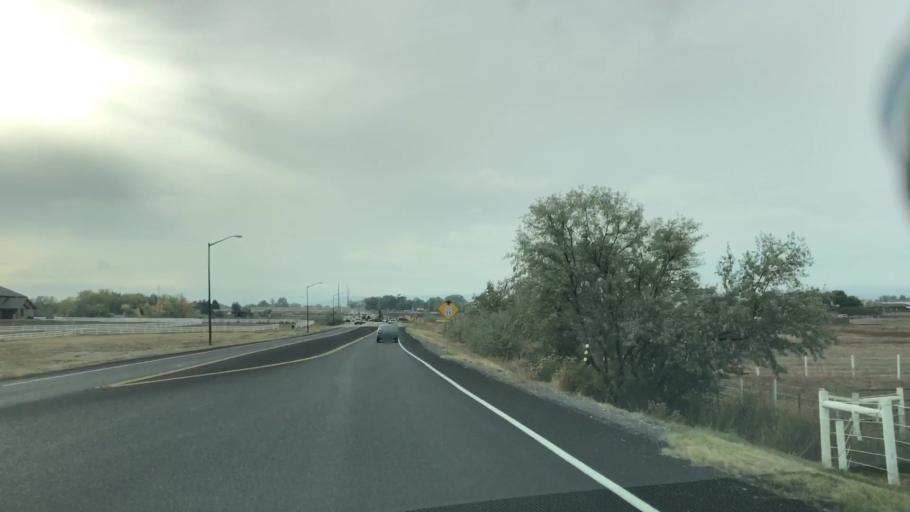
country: US
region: Colorado
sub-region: Larimer County
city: Loveland
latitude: 40.4656
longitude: -105.0351
